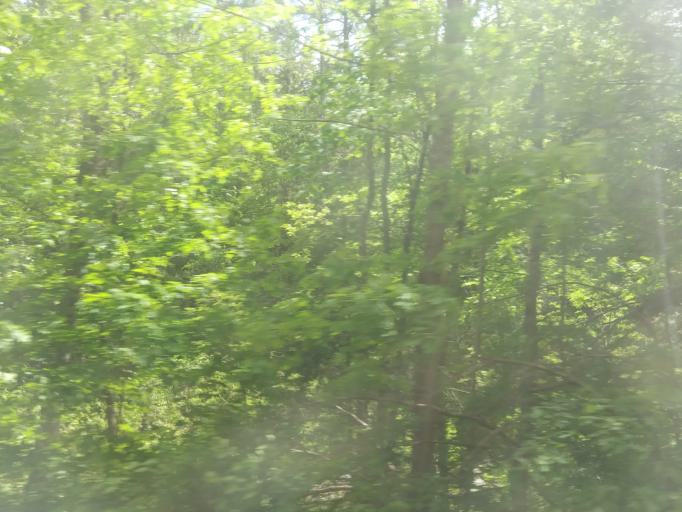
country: US
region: Massachusetts
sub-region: Franklin County
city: Buckland
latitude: 42.5806
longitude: -72.8231
